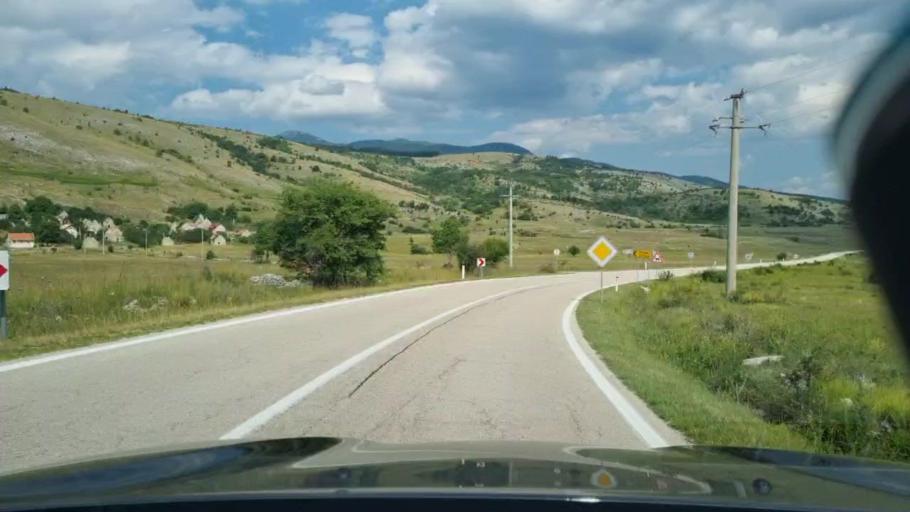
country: BA
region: Federation of Bosnia and Herzegovina
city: Bosansko Grahovo
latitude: 44.1319
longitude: 16.5062
